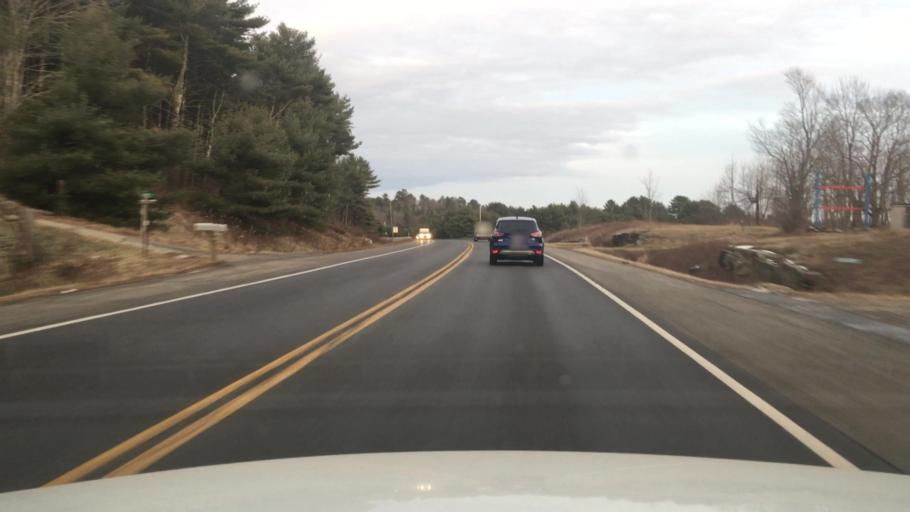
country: US
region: Maine
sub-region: Lincoln County
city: Edgecomb
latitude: 44.0129
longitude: -69.5885
